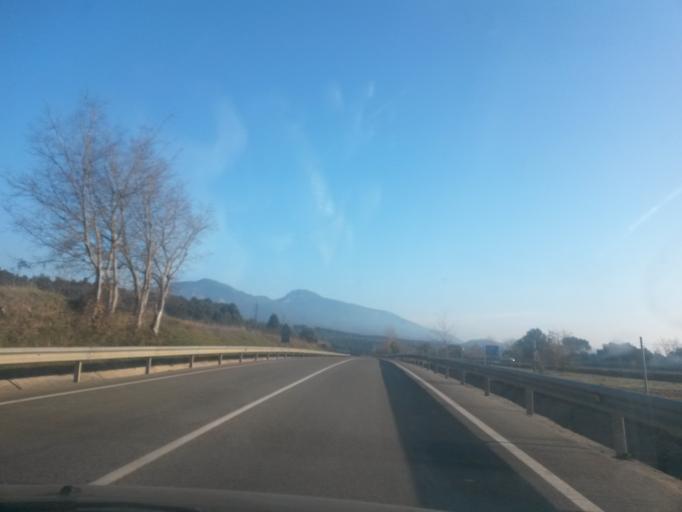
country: ES
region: Catalonia
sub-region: Provincia de Girona
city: Argelaguer
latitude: 42.2137
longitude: 2.6254
